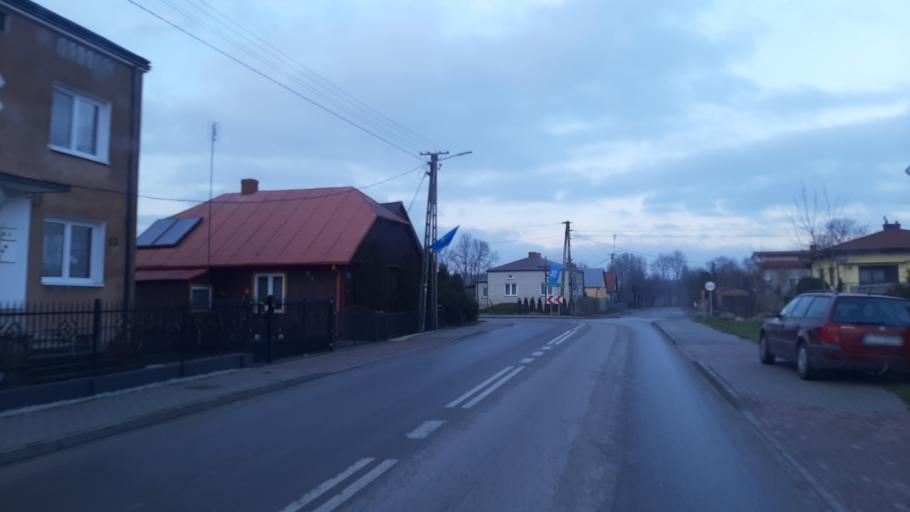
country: PL
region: Lublin Voivodeship
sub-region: Powiat lubartowski
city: Kamionka
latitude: 51.4717
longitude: 22.4629
